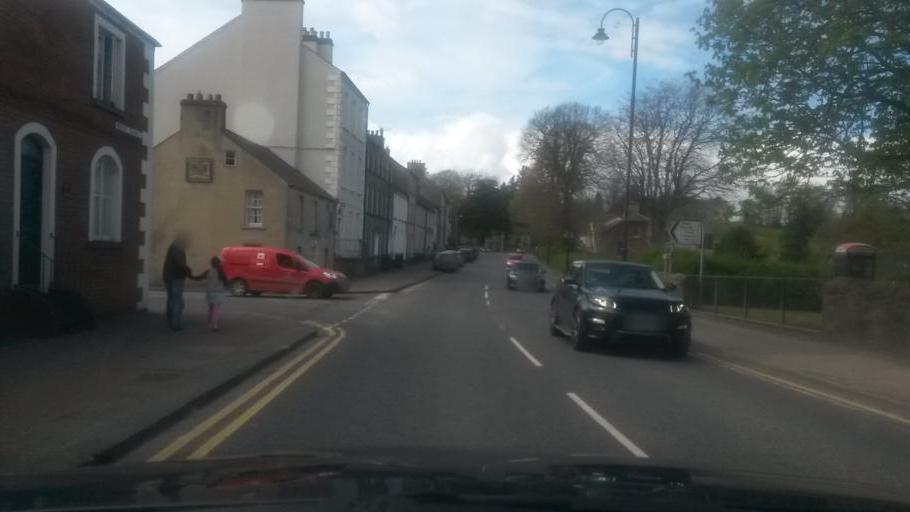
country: GB
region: Northern Ireland
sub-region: Fermanagh District
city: Enniskillen
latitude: 54.3485
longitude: -7.6499
